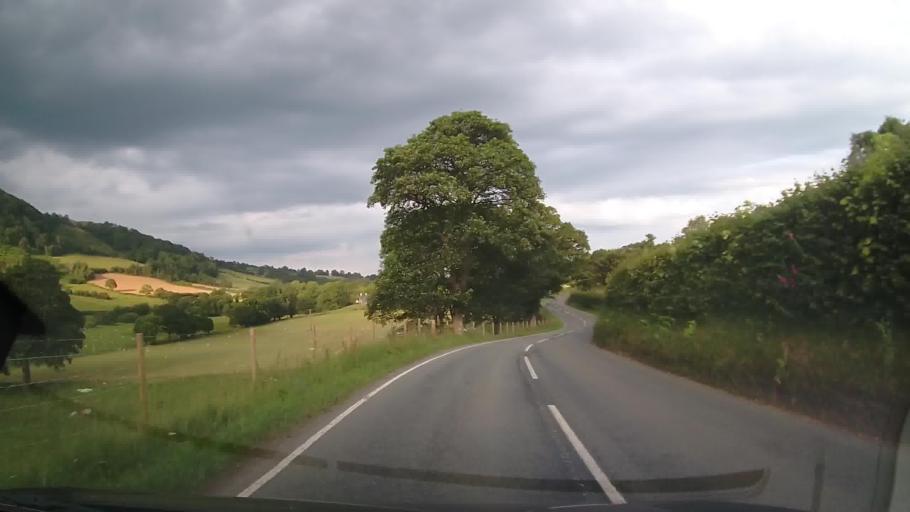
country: GB
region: Wales
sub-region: Sir Powys
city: Llangynog
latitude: 52.8212
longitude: -3.3829
